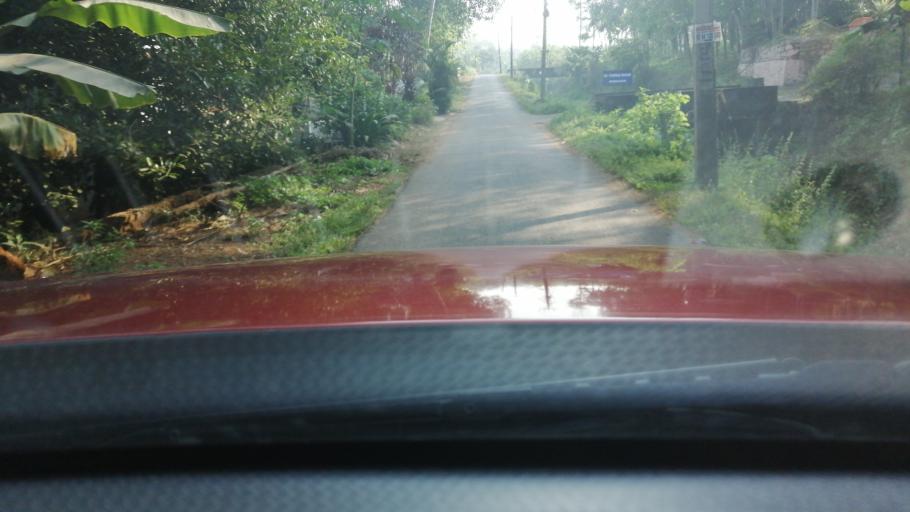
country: IN
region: Kerala
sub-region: Ernakulam
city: Piravam
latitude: 9.8945
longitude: 76.4443
